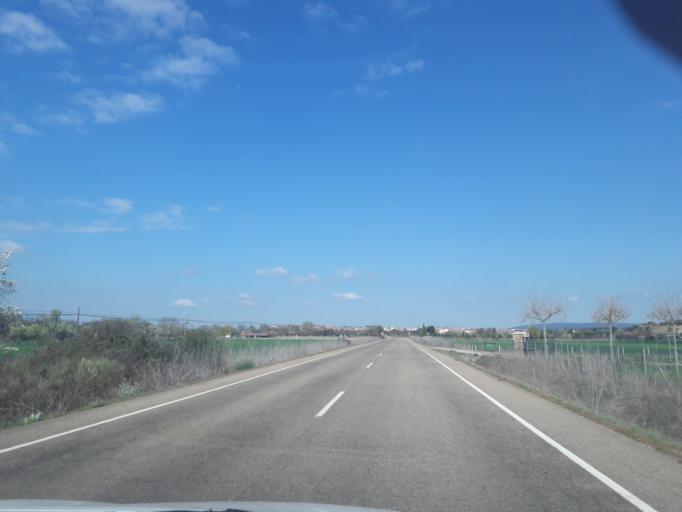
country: ES
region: Castille and Leon
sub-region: Provincia de Salamanca
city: Ciudad Rodrigo
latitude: 40.5785
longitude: -6.5025
